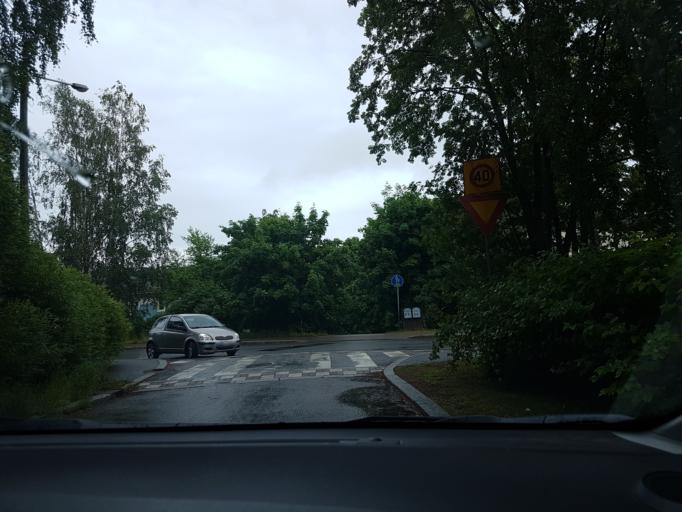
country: FI
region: Uusimaa
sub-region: Helsinki
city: Vantaa
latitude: 60.2298
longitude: 25.0977
